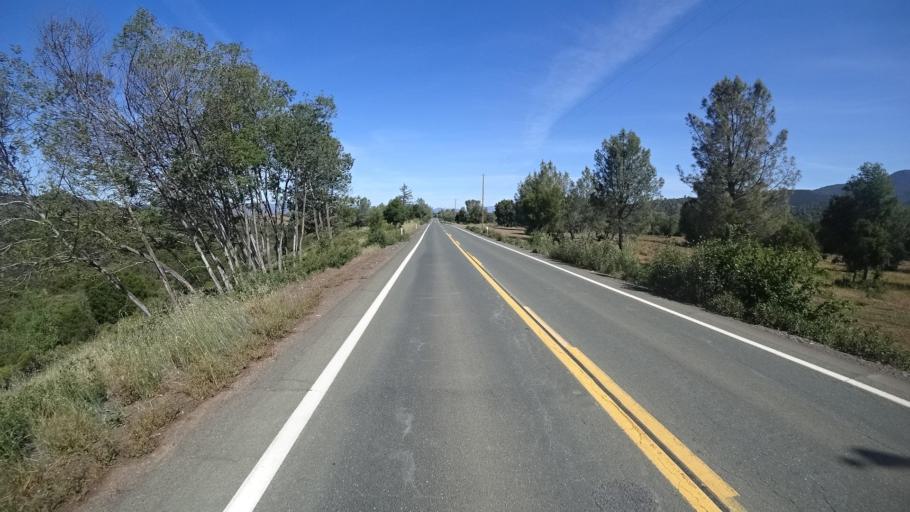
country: US
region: California
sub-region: Lake County
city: Kelseyville
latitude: 38.9333
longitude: -122.8102
